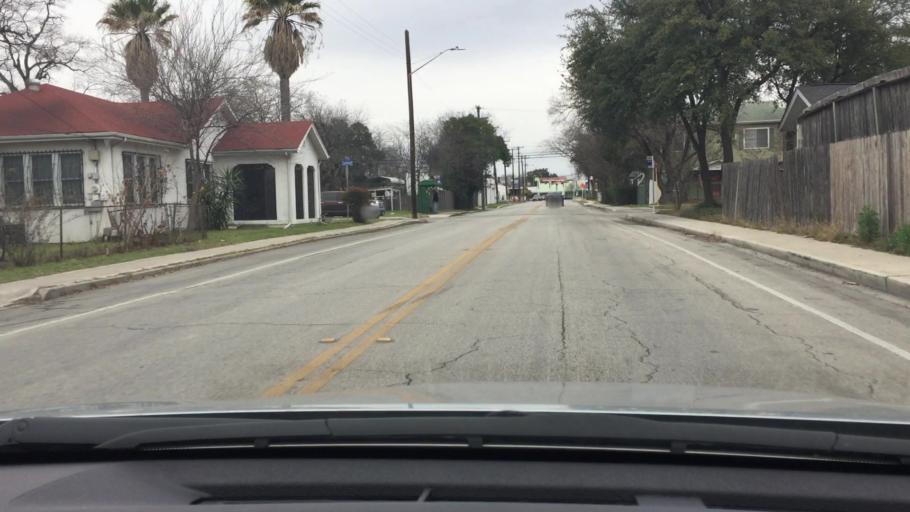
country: US
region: Texas
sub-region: Bexar County
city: Balcones Heights
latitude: 29.4587
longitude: -98.5232
